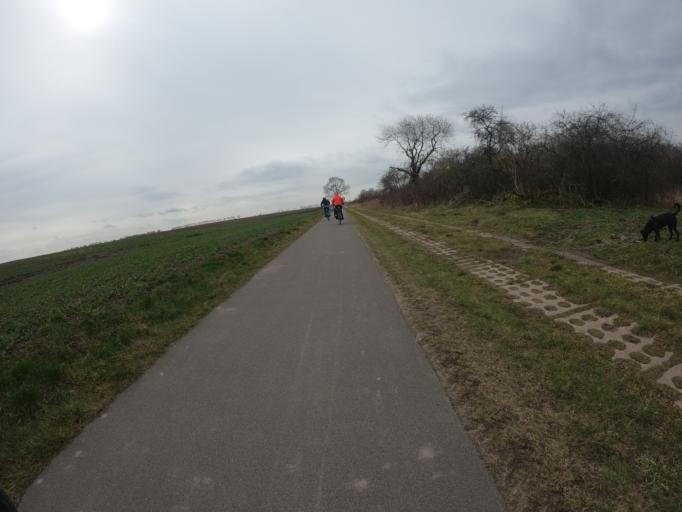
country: PL
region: West Pomeranian Voivodeship
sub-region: Powiat gryficki
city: Mrzezyno
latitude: 54.1119
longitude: 15.2978
